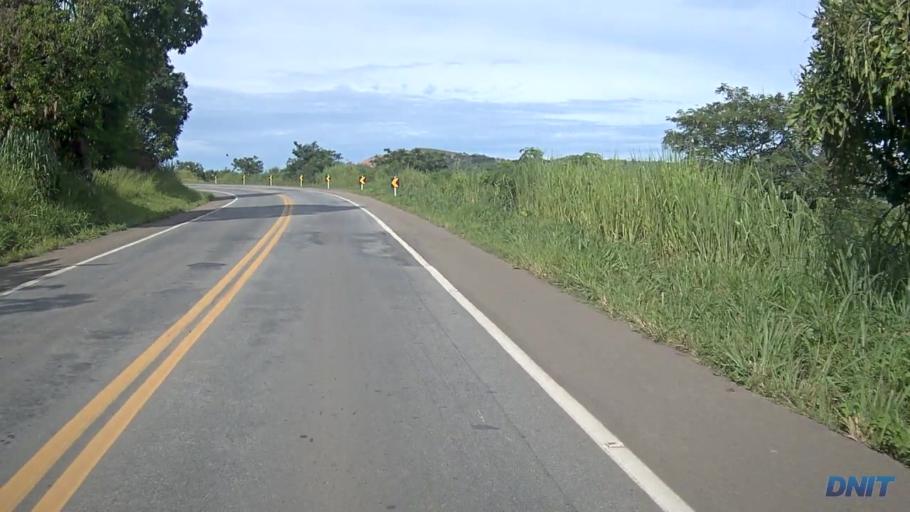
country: BR
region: Minas Gerais
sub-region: Belo Oriente
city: Belo Oriente
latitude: -19.1647
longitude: -42.2431
